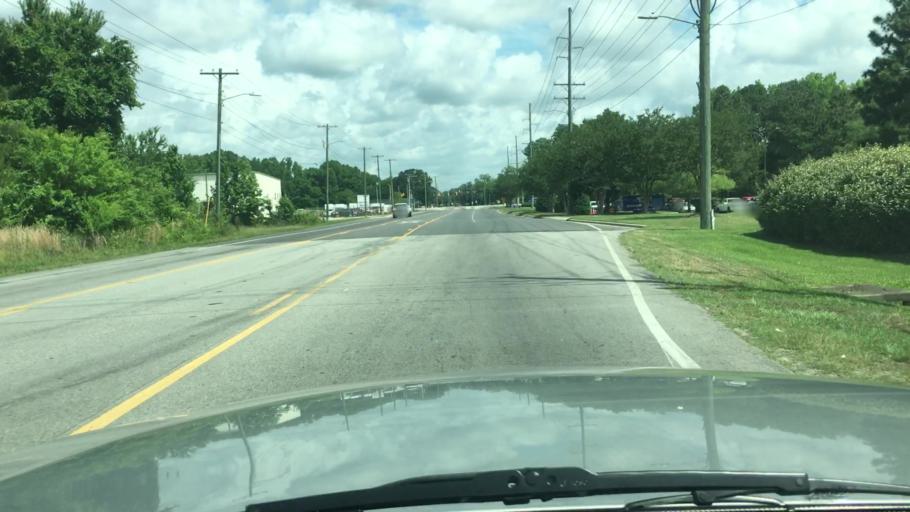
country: US
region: North Carolina
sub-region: Cumberland County
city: Fayetteville
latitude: 35.0320
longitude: -78.8724
